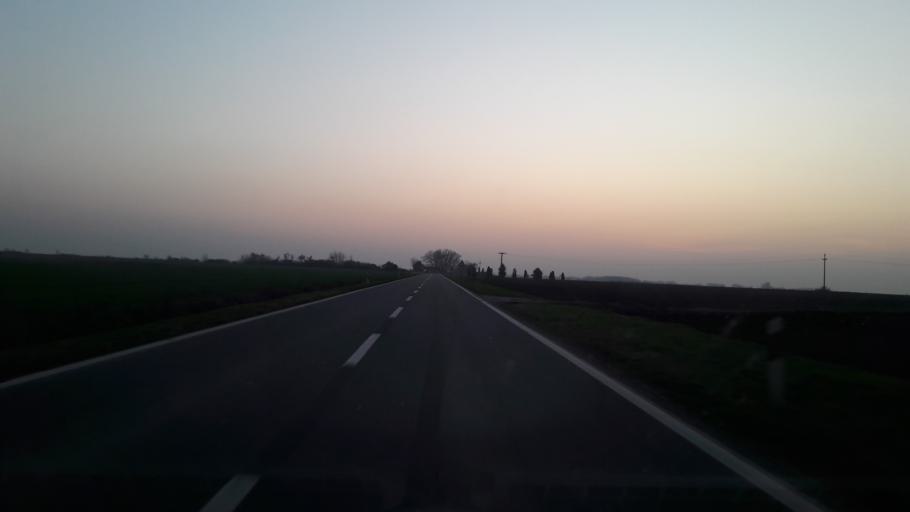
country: HR
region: Vukovarsko-Srijemska
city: Negoslavci
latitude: 45.2648
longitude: 18.9899
